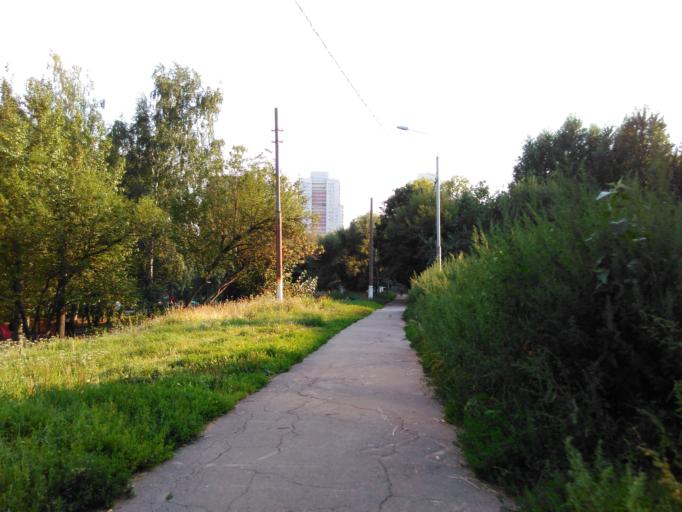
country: RU
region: Moscow
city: Zyuzino
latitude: 55.6418
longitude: 37.5449
